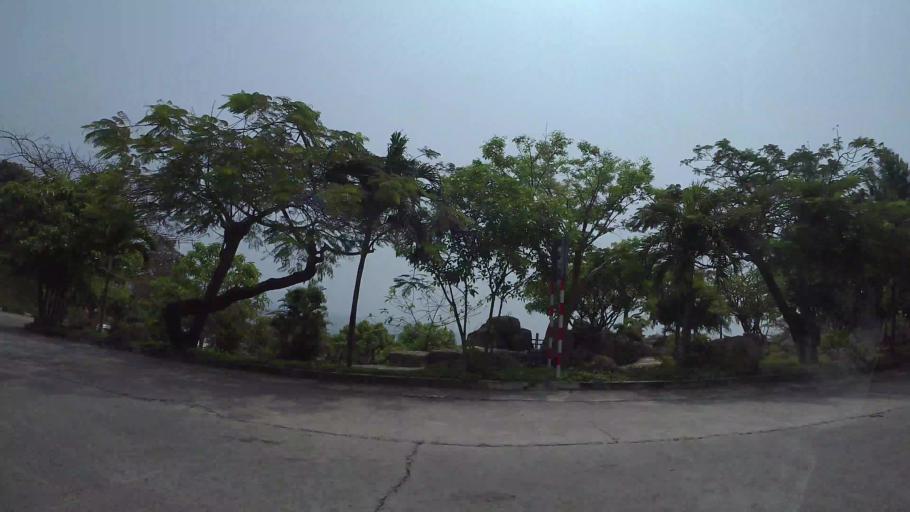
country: VN
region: Da Nang
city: Son Tra
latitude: 16.0993
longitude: 108.2789
